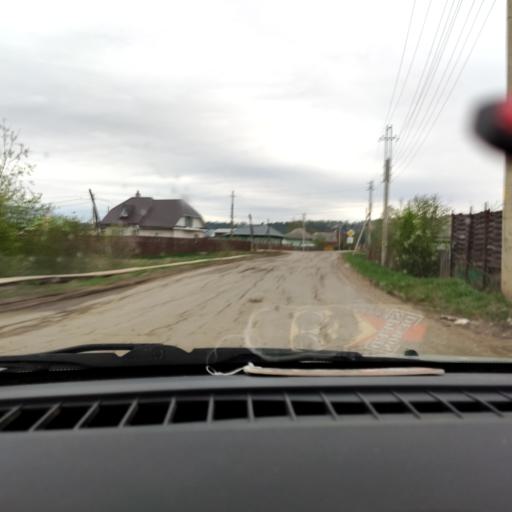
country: RU
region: Perm
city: Kudymkar
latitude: 59.0087
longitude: 54.6433
